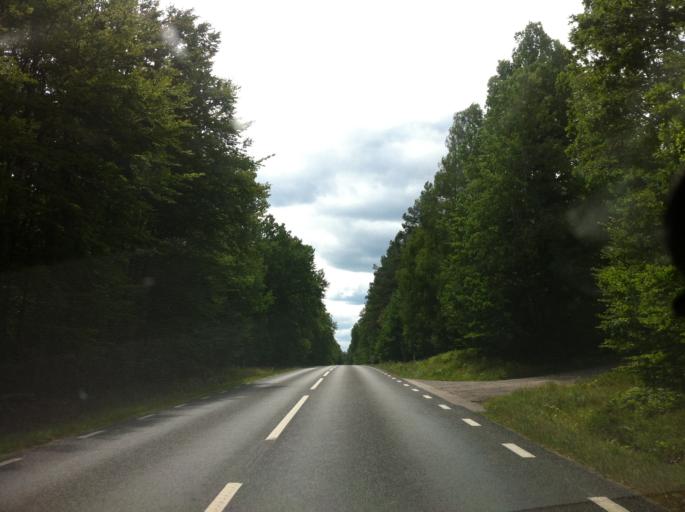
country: SE
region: Kalmar
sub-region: Emmaboda Kommun
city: Emmaboda
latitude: 56.6021
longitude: 15.4541
